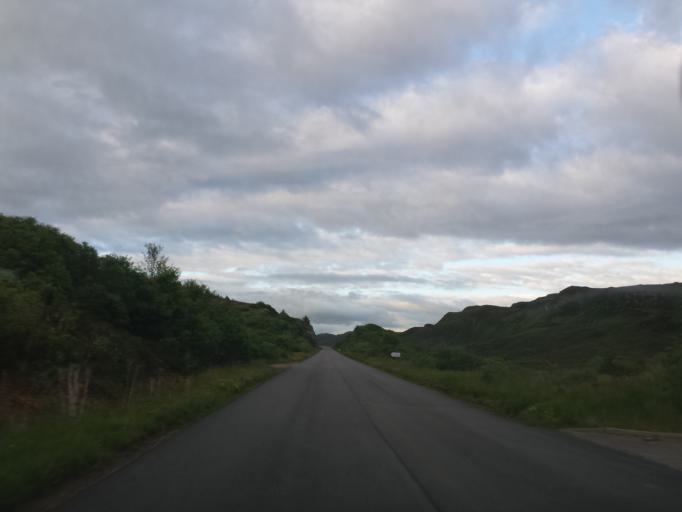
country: GB
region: Scotland
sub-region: Highland
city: Portree
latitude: 57.3067
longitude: -5.5615
